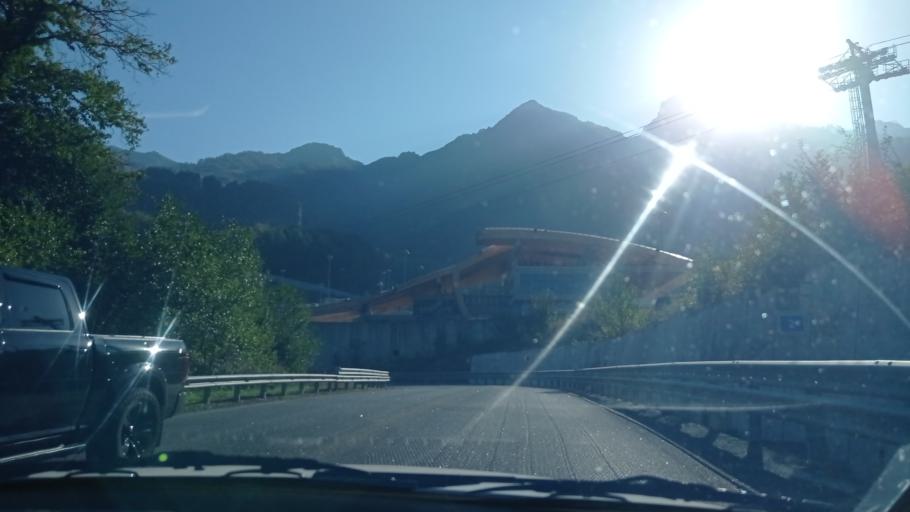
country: RU
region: Krasnodarskiy
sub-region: Sochi City
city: Krasnaya Polyana
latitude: 43.6689
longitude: 40.2895
